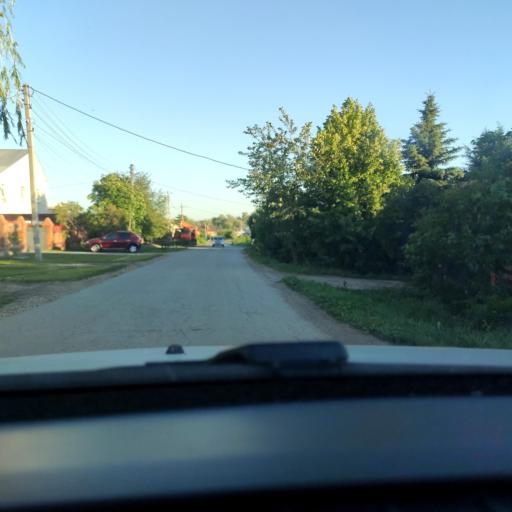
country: RU
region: Samara
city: Kinel'
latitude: 53.2697
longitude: 50.5926
